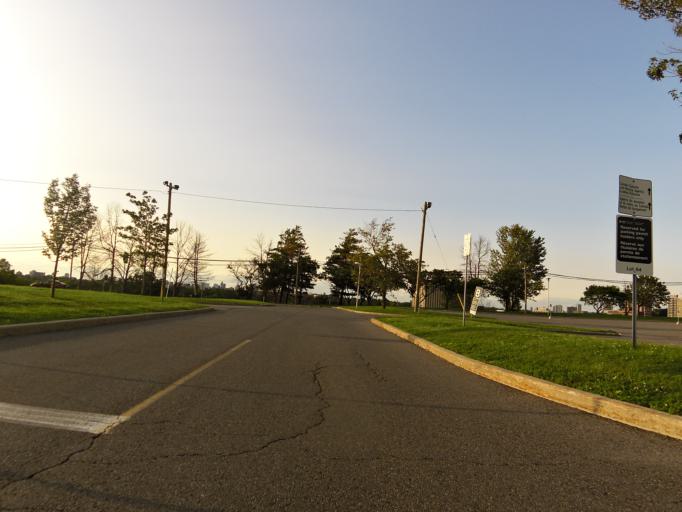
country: CA
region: Ontario
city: Ottawa
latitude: 45.3809
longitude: -75.6808
